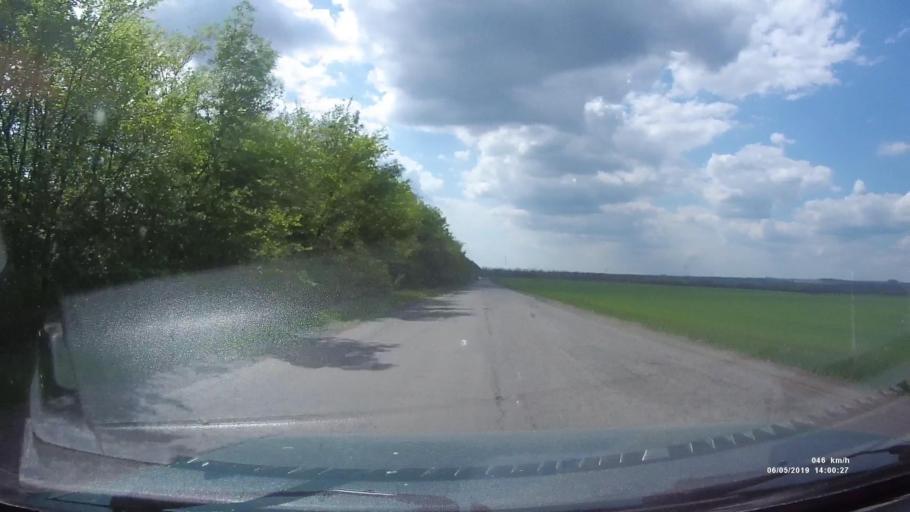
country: RU
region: Rostov
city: Shakhty
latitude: 47.6853
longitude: 40.3888
